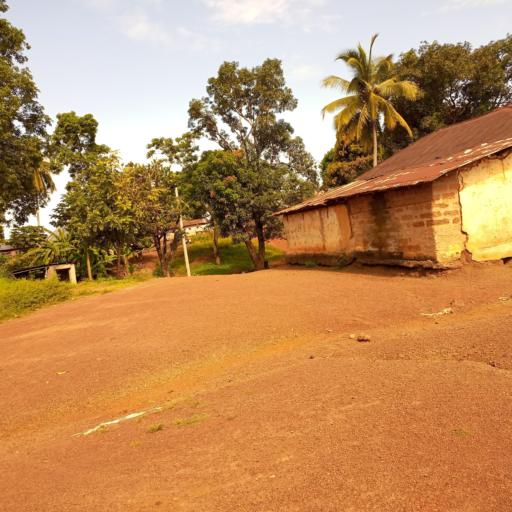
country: SL
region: Northern Province
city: Kambia
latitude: 9.1218
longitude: -12.9153
